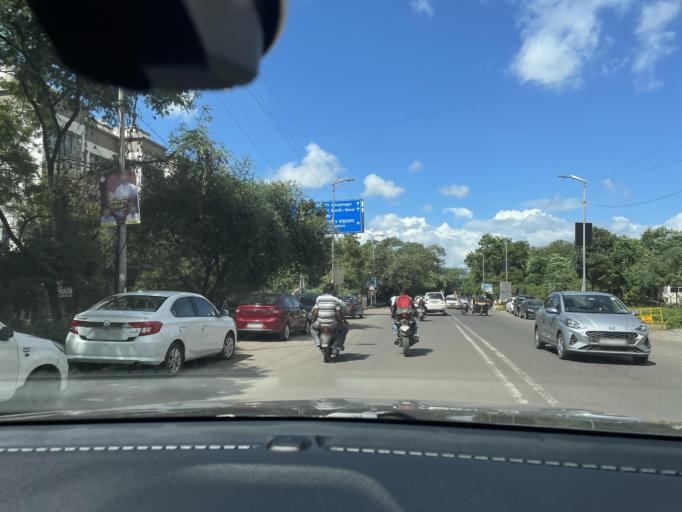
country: IN
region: Maharashtra
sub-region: Pune Division
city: Shivaji Nagar
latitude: 18.5234
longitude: 73.7802
